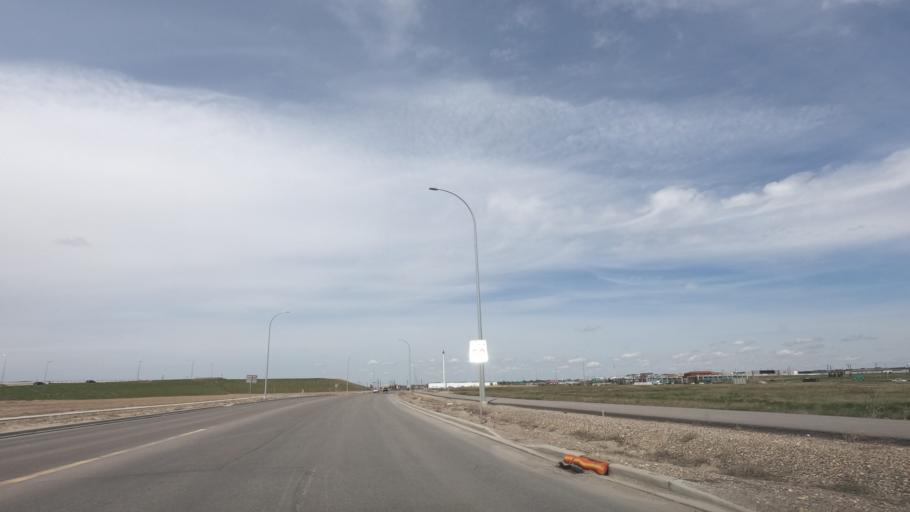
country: CA
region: Alberta
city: Airdrie
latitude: 51.2531
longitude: -114.0049
